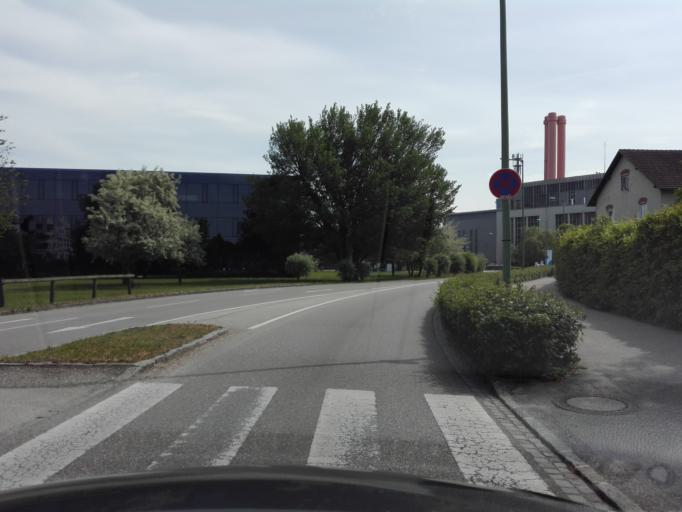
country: AT
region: Upper Austria
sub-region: Wels-Land
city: Thalheim bei Wels
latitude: 48.1534
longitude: 14.0080
